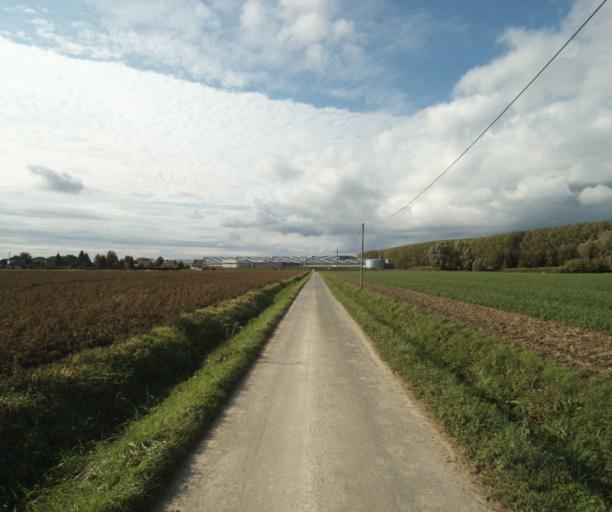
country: FR
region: Nord-Pas-de-Calais
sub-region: Departement du Nord
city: Ennetieres-en-Weppes
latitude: 50.6485
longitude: 2.9181
